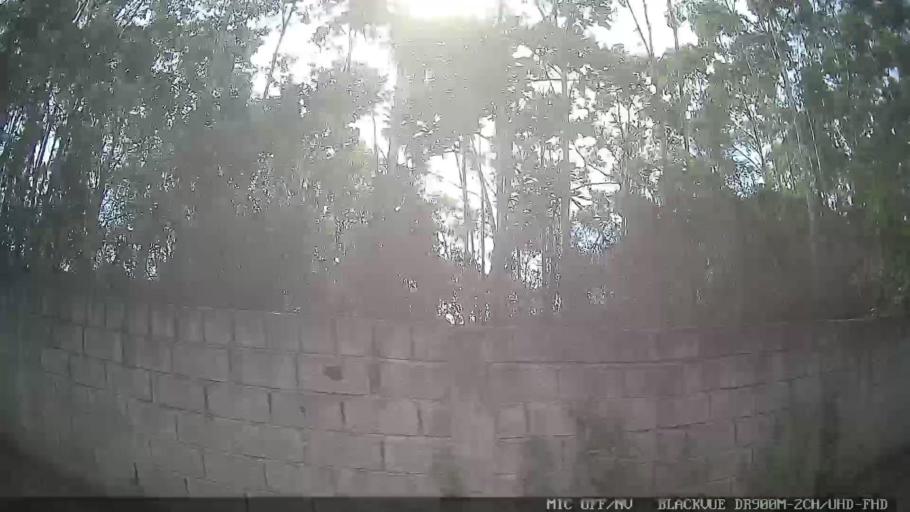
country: BR
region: Sao Paulo
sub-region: Jarinu
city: Jarinu
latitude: -23.0562
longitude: -46.6415
